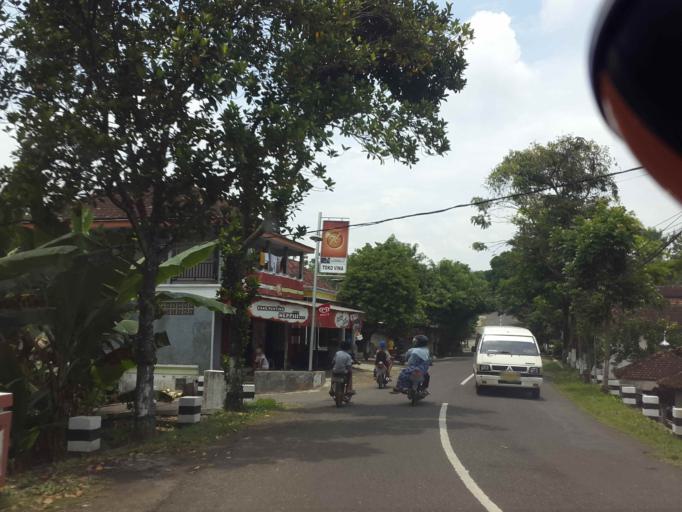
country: ID
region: East Java
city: Madiun
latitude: -7.6884
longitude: 111.3387
